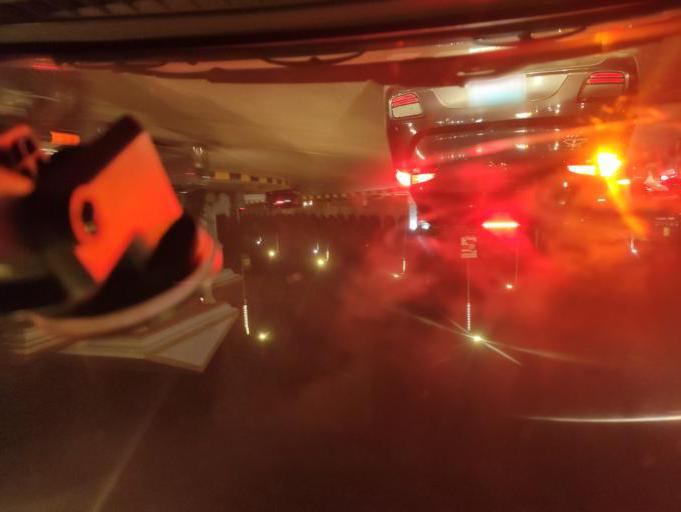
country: EG
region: Al Jizah
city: Awsim
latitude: 30.0227
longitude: 31.0049
